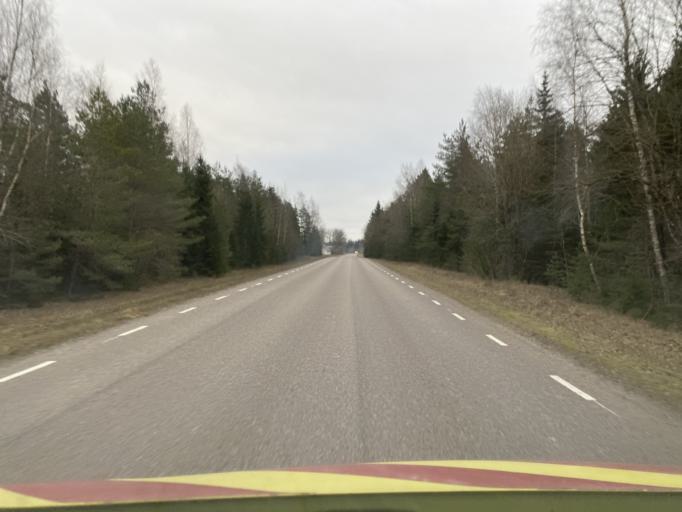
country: EE
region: Laeaene
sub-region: Ridala Parish
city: Uuemoisa
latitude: 59.0203
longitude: 23.6718
